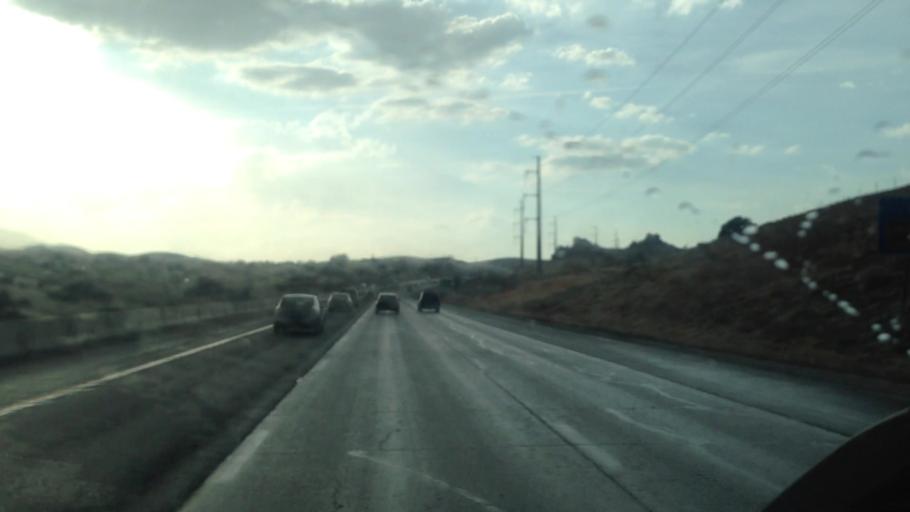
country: US
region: Nevada
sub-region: Washoe County
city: Golden Valley
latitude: 39.5777
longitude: -119.8130
